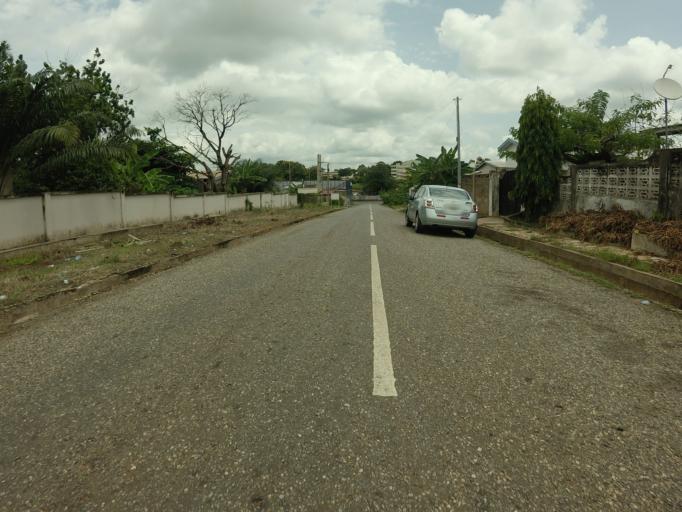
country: GH
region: Volta
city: Ho
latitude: 6.5918
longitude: 0.4732
